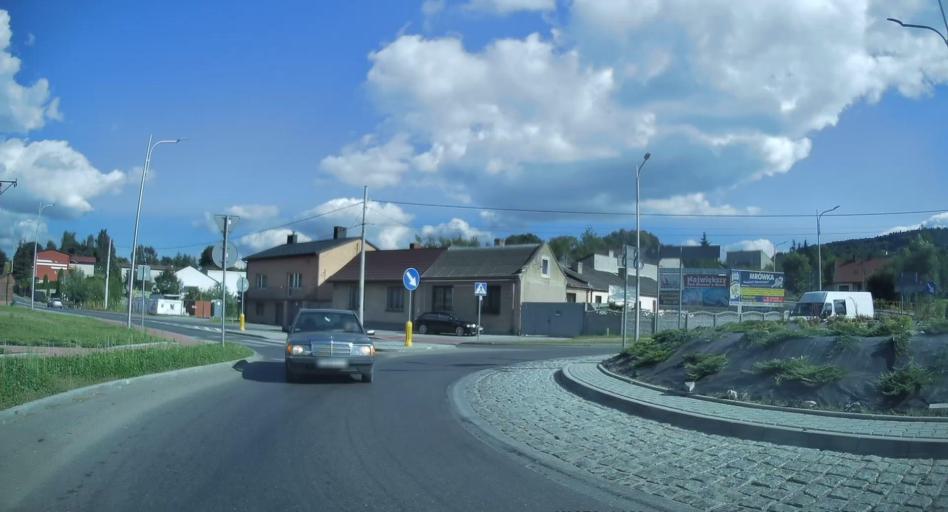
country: PL
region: Swietokrzyskie
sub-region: Powiat kielecki
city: Bodzentyn
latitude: 50.9396
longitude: 20.9499
